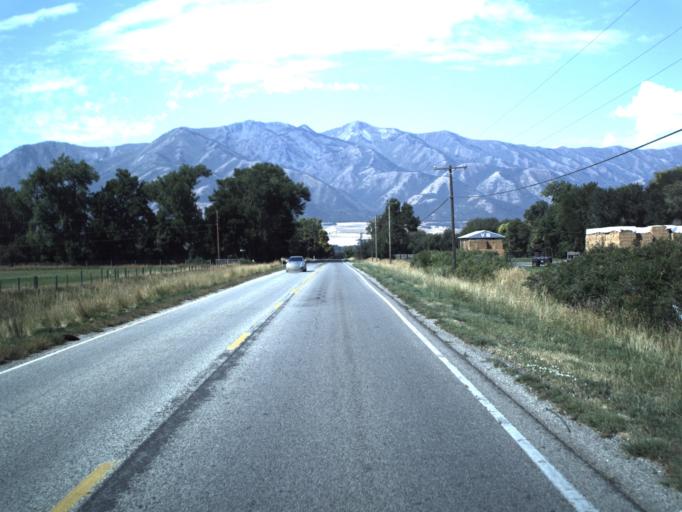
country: US
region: Utah
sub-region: Cache County
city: Hyrum
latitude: 41.6410
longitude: -111.8888
